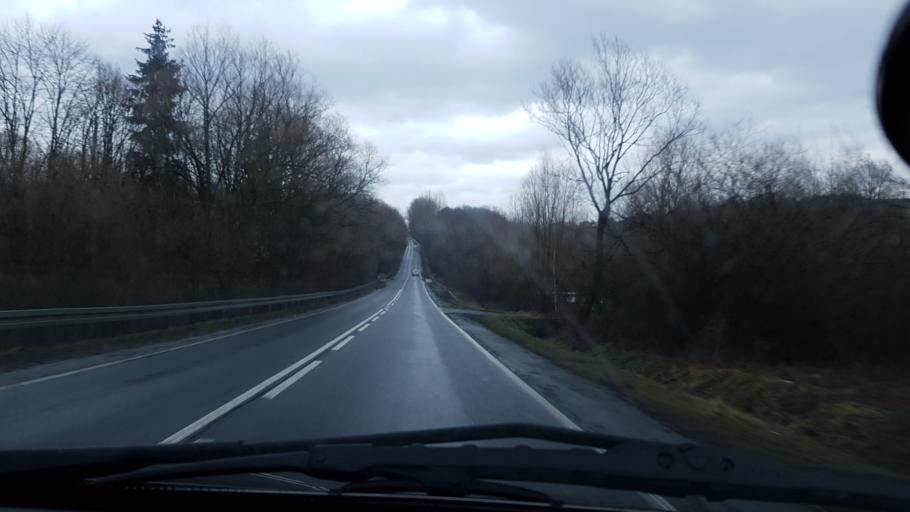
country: PL
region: Silesian Voivodeship
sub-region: Powiat zywiecki
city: Zywiec
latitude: 49.7111
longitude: 19.2160
